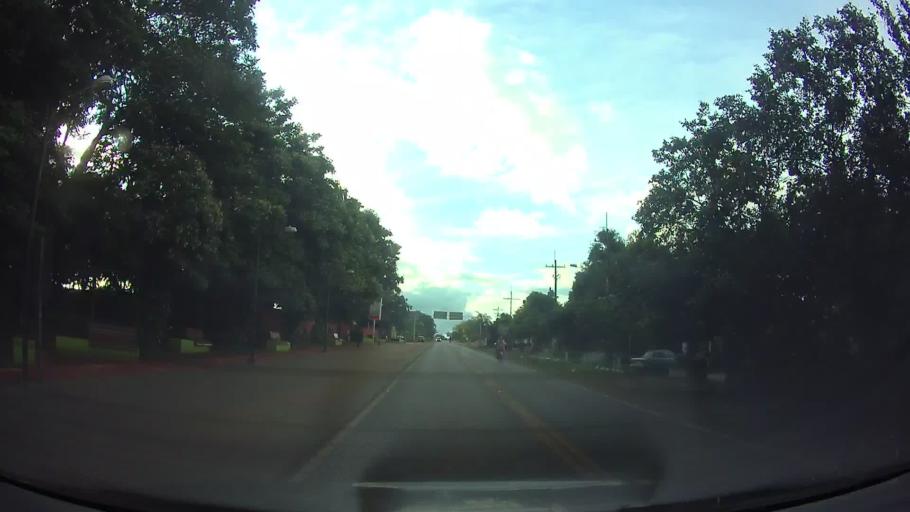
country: PY
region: Paraguari
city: Ybycui
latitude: -26.0140
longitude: -57.0294
